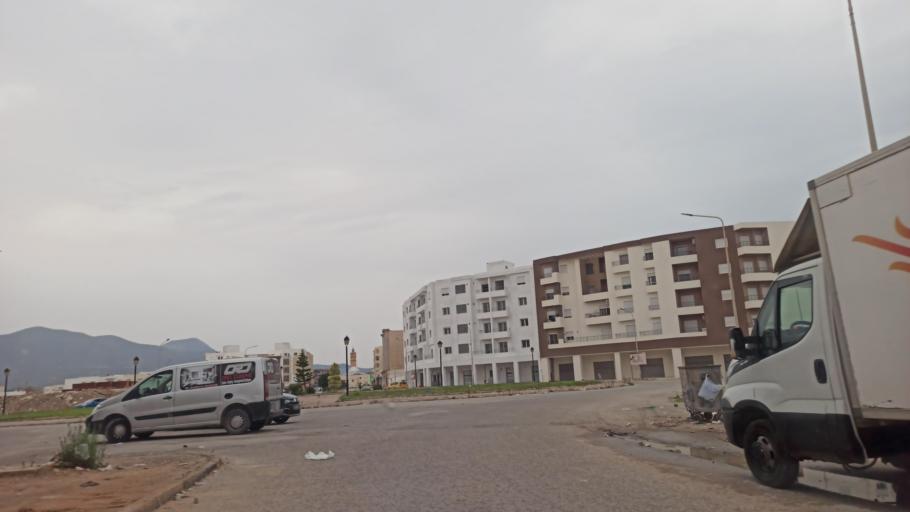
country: TN
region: Tunis
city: Hammam-Lif
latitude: 36.7051
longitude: 10.4145
